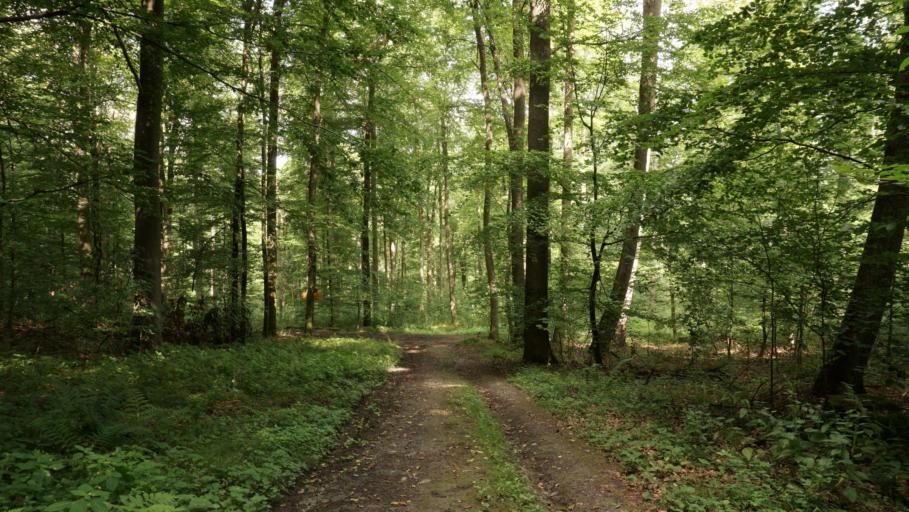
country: DE
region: Baden-Wuerttemberg
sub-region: Karlsruhe Region
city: Mosbach
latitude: 49.3344
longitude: 9.1621
